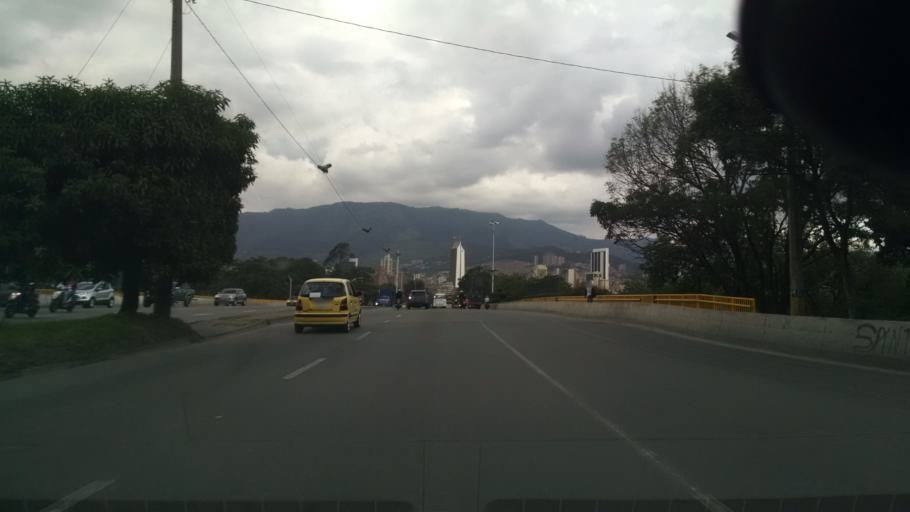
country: CO
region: Antioquia
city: Medellin
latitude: 6.2616
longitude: -75.5743
